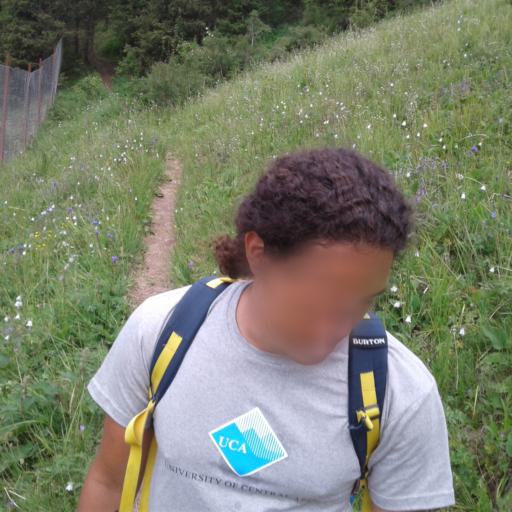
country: KG
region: Naryn
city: Naryn
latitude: 41.4555
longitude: 76.4523
